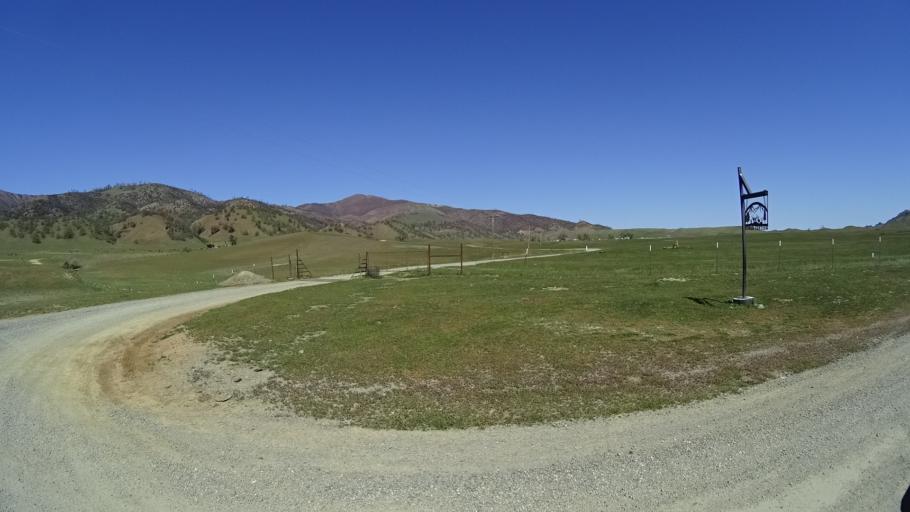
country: US
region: California
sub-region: Tehama County
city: Rancho Tehama Reserve
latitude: 39.6991
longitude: -122.5630
